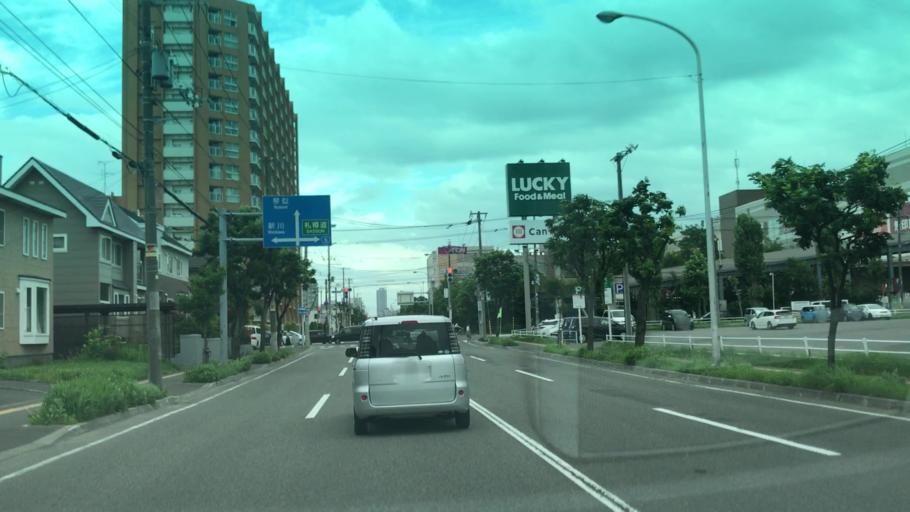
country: JP
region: Hokkaido
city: Sapporo
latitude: 43.0983
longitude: 141.2759
